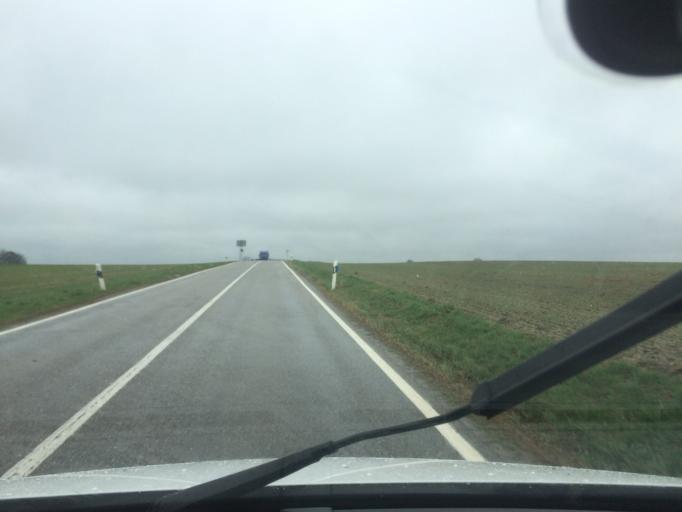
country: DE
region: Bavaria
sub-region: Upper Bavaria
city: Assling
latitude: 47.9659
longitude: 11.9627
